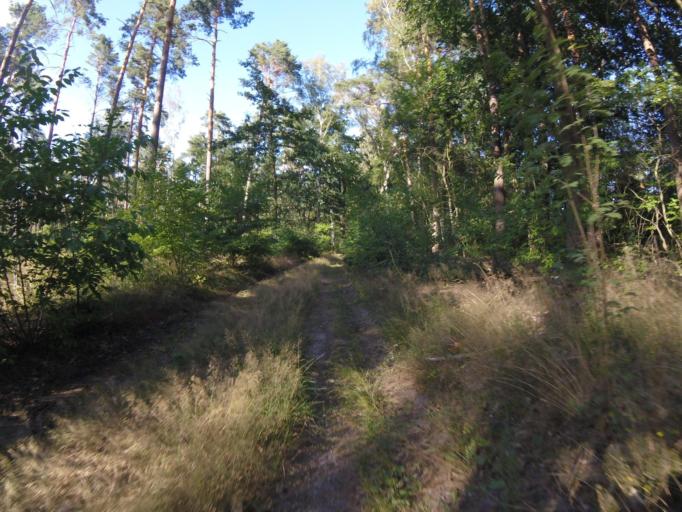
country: DE
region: Berlin
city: Schmockwitz
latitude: 52.3268
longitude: 13.7257
